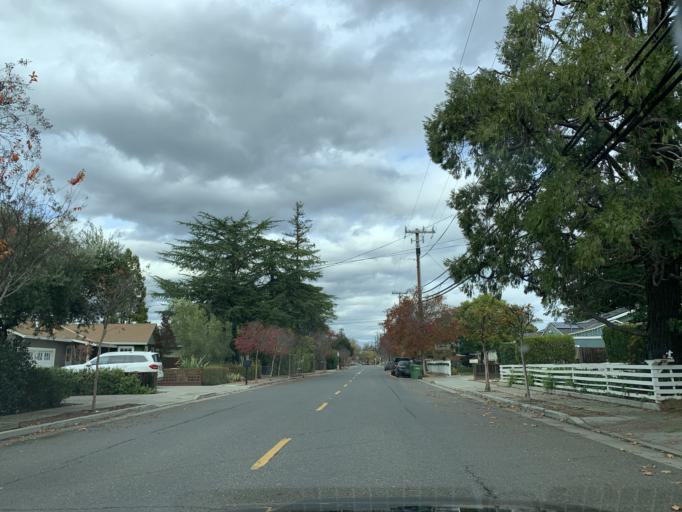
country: US
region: California
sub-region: Santa Clara County
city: Campbell
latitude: 37.2703
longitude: -121.9720
